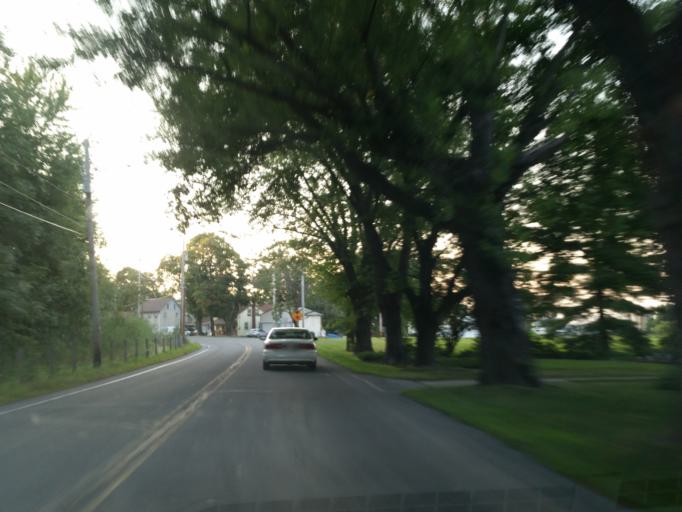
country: US
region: Pennsylvania
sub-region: Lebanon County
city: Newmanstown
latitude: 40.2996
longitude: -76.2468
